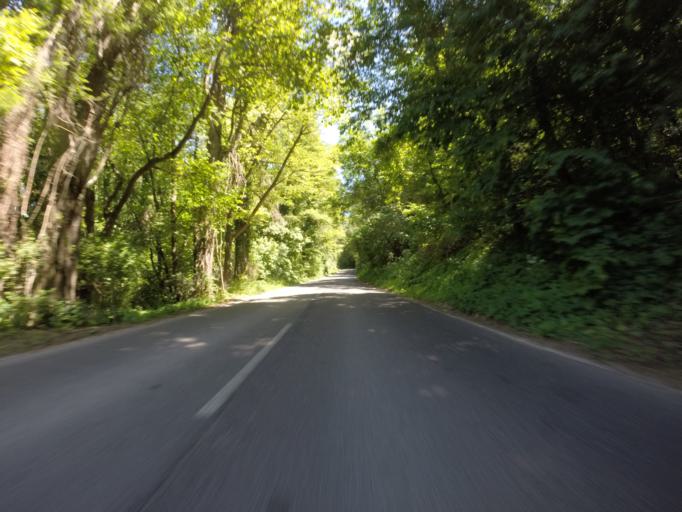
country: SK
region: Trnavsky
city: Hlohovec
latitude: 48.4612
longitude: 17.8292
